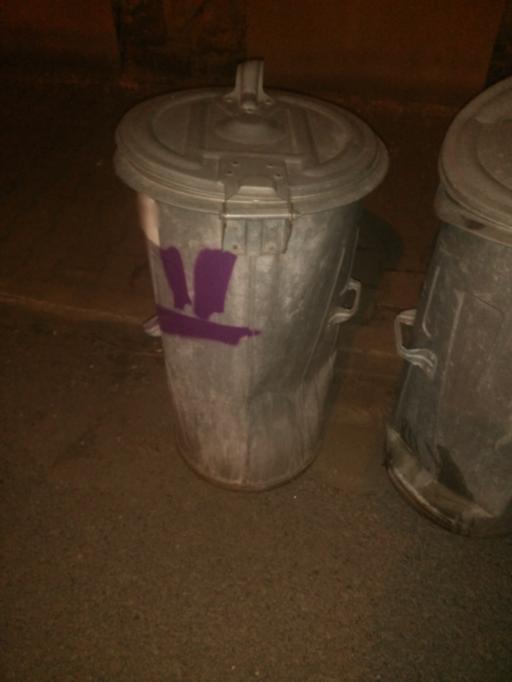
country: CZ
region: Moravskoslezsky
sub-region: Okres Novy Jicin
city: Novy Jicin
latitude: 49.5985
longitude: 18.0159
